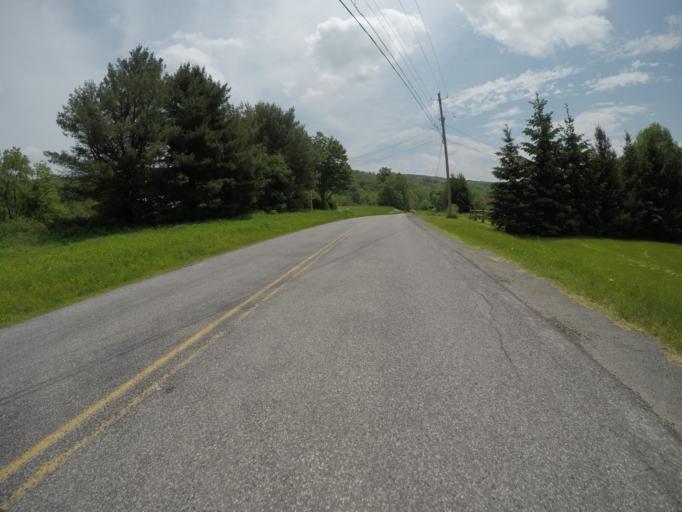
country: US
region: New York
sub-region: Delaware County
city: Stamford
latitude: 42.1875
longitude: -74.6726
